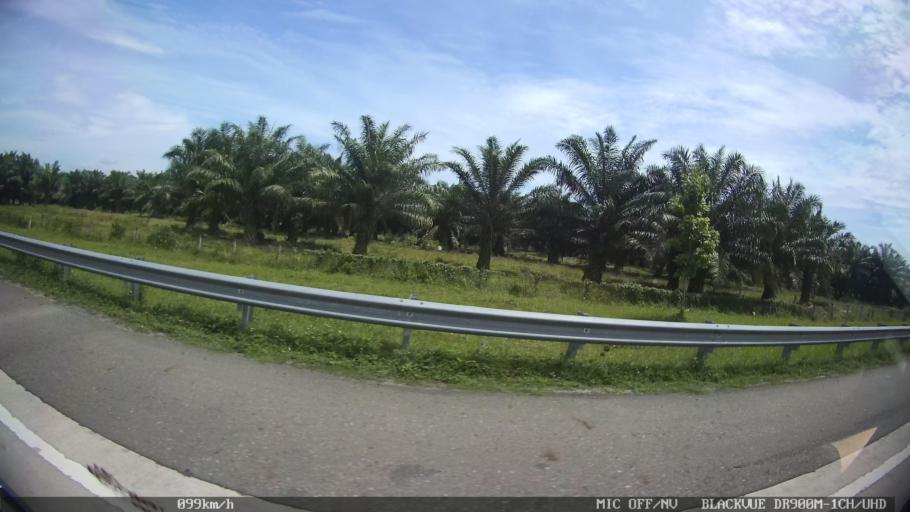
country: ID
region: North Sumatra
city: Perbaungan
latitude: 3.5316
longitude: 98.8797
